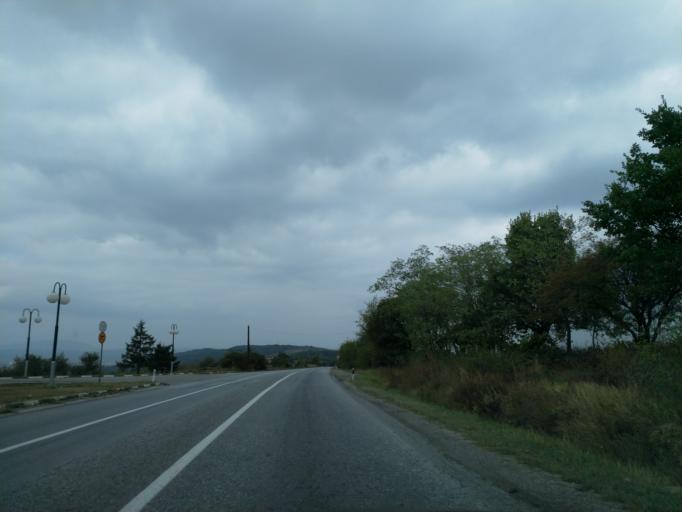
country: RS
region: Central Serbia
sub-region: Sumadijski Okrug
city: Topola
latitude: 44.1442
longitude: 20.7426
